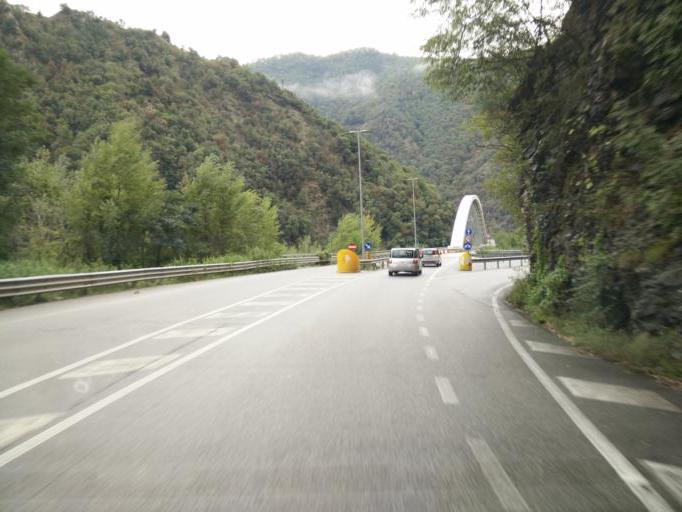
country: IT
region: Tuscany
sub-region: Provincia di Lucca
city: Valdottavo
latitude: 43.9334
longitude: 10.5077
